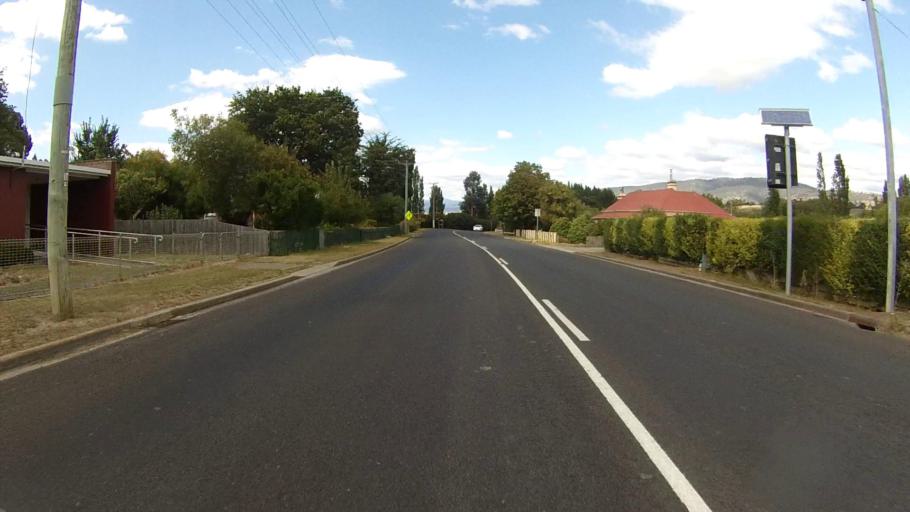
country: AU
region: Tasmania
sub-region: Derwent Valley
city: New Norfolk
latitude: -42.6977
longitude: 146.8898
